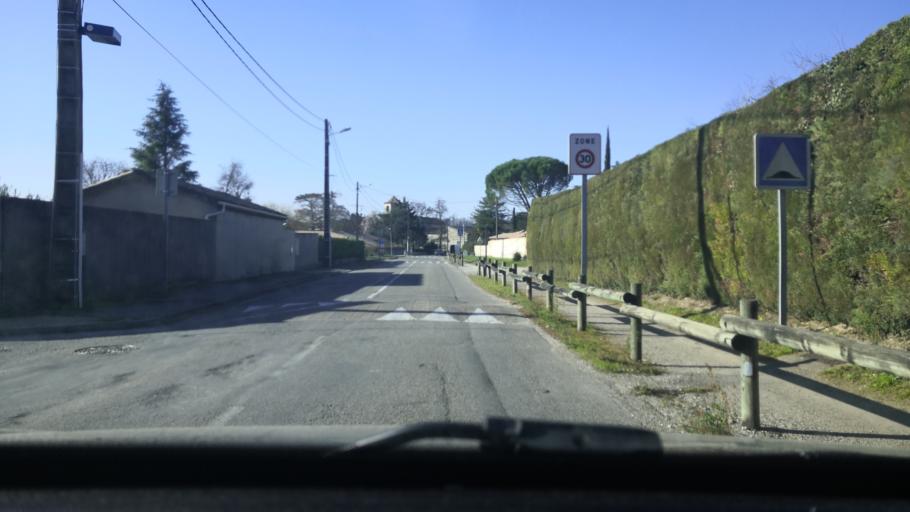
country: FR
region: Rhone-Alpes
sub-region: Departement de la Drome
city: Saint-Marcel-les-Sauzet
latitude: 44.5977
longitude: 4.8082
